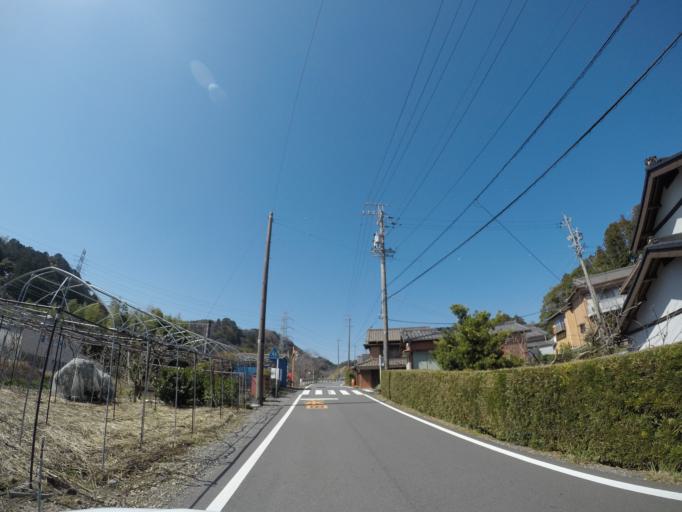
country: JP
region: Shizuoka
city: Kanaya
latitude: 34.7939
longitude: 138.1261
